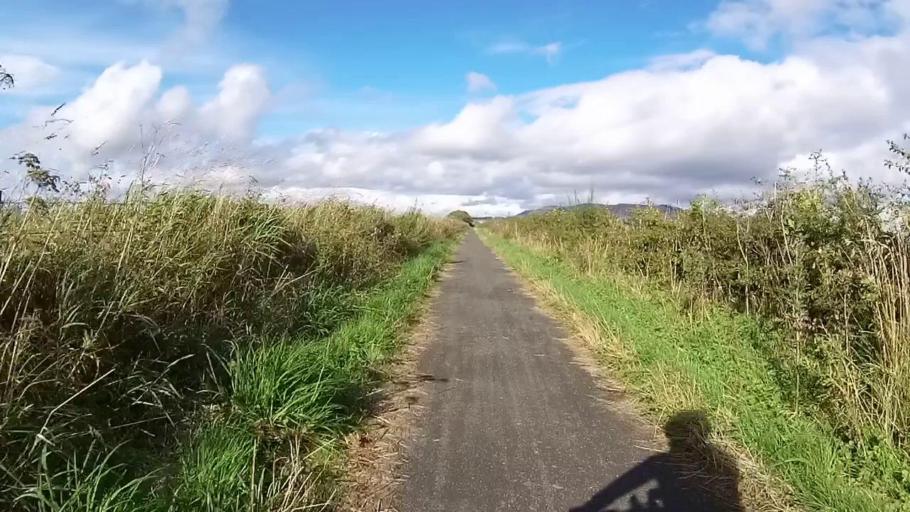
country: GB
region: Scotland
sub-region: Perth and Kinross
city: Kinross
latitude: 56.1793
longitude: -3.3870
